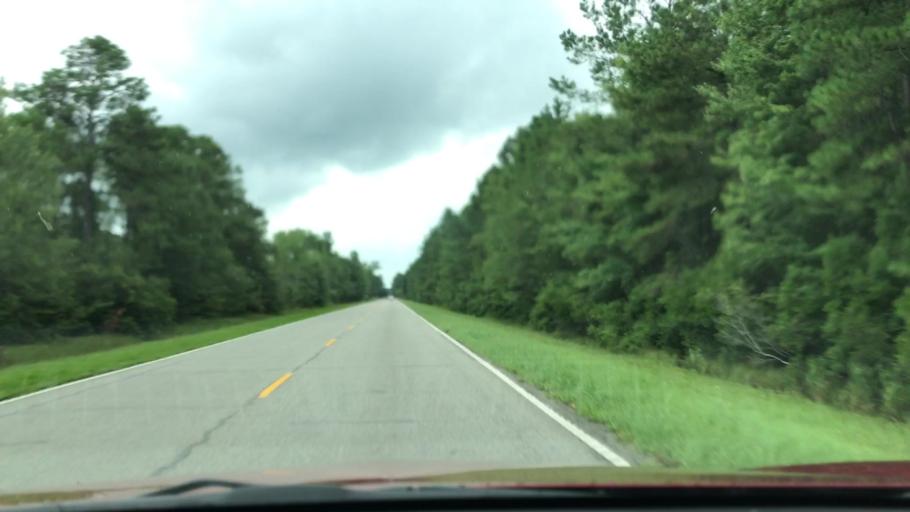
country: US
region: South Carolina
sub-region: Georgetown County
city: Georgetown
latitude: 33.5386
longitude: -79.2313
